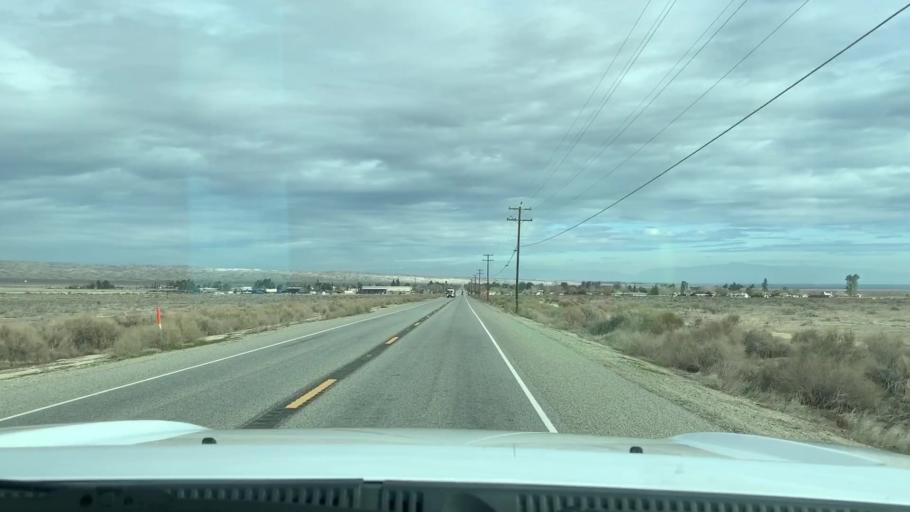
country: US
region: California
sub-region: Kern County
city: Ford City
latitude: 35.2003
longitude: -119.4186
